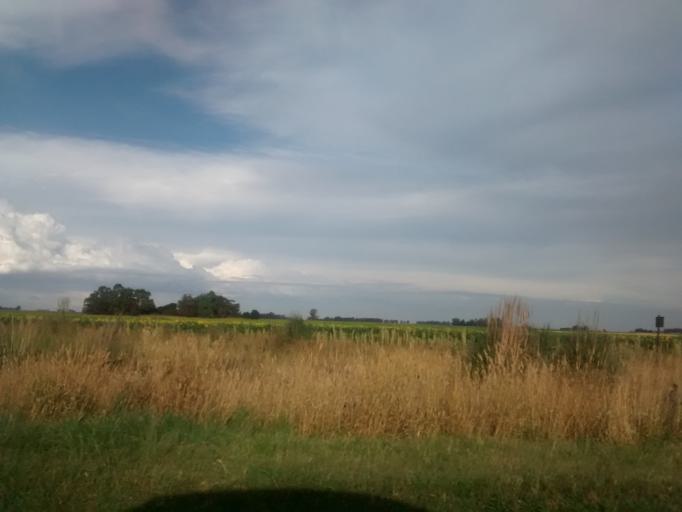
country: AR
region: Buenos Aires
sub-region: Partido de Loberia
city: Loberia
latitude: -38.2145
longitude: -58.7323
